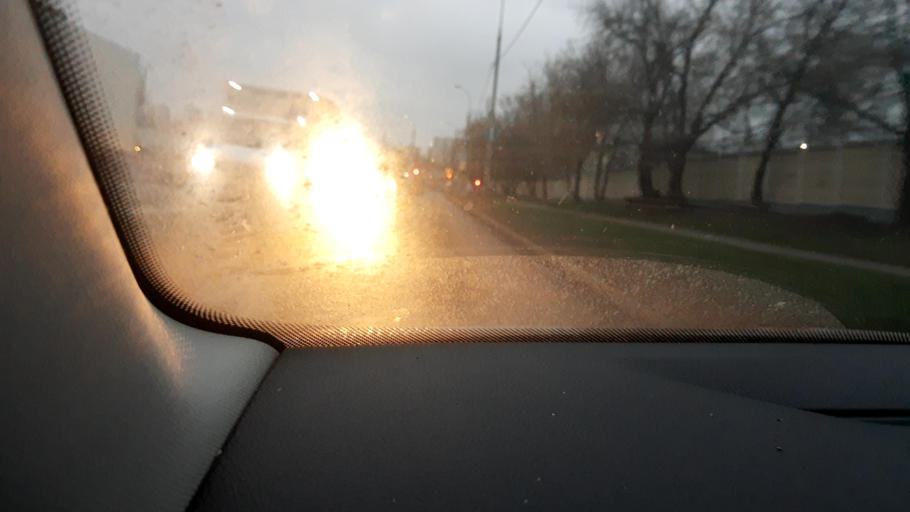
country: RU
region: Moscow
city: Tsaritsyno
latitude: 55.6461
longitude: 37.6399
